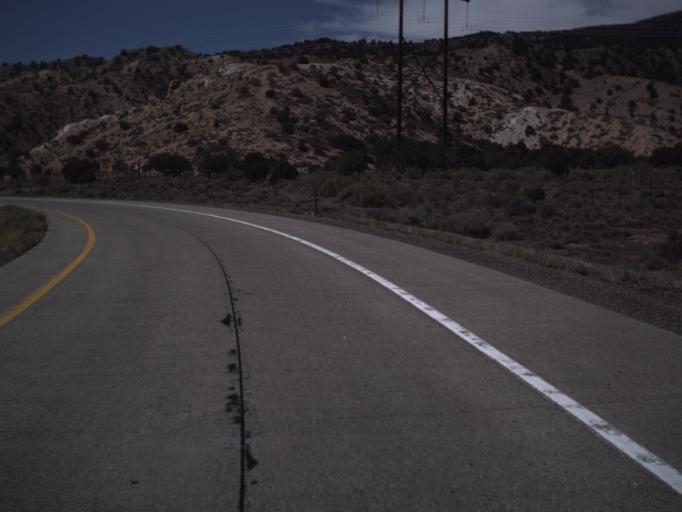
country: US
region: Utah
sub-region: Sevier County
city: Monroe
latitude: 38.6034
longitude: -112.2519
